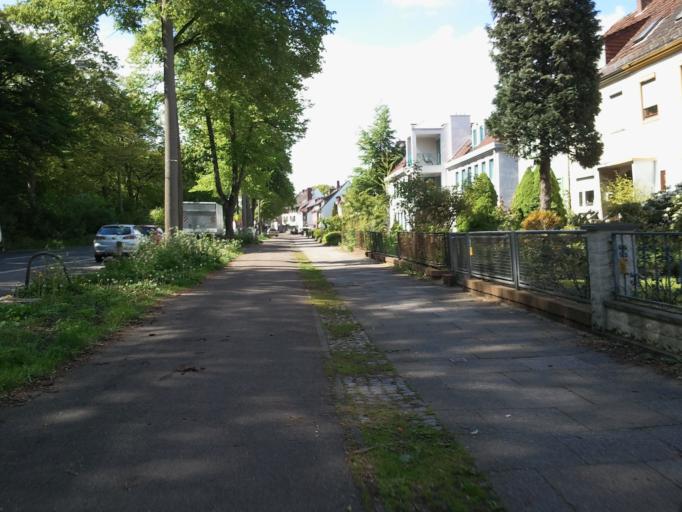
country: DE
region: Lower Saxony
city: Ritterhude
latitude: 53.1306
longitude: 8.7424
